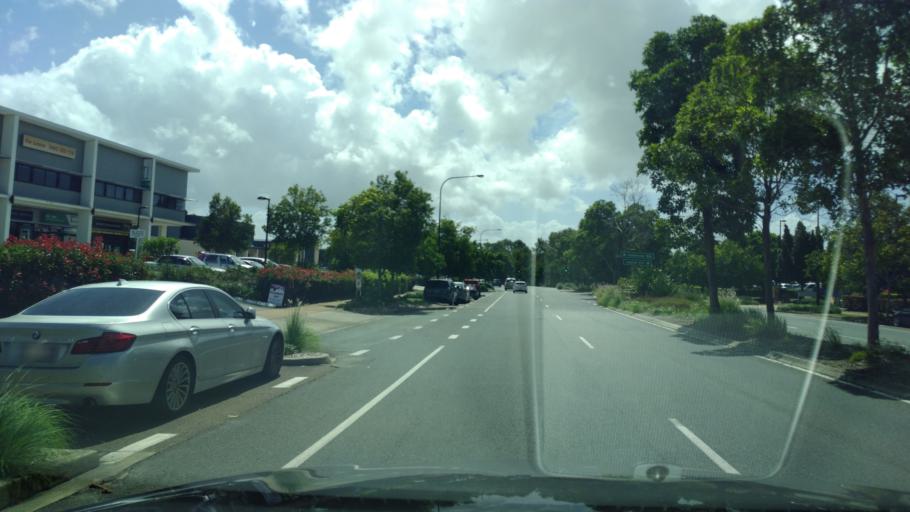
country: AU
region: Queensland
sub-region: Moreton Bay
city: Mango Hill
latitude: -27.2397
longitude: 153.0236
